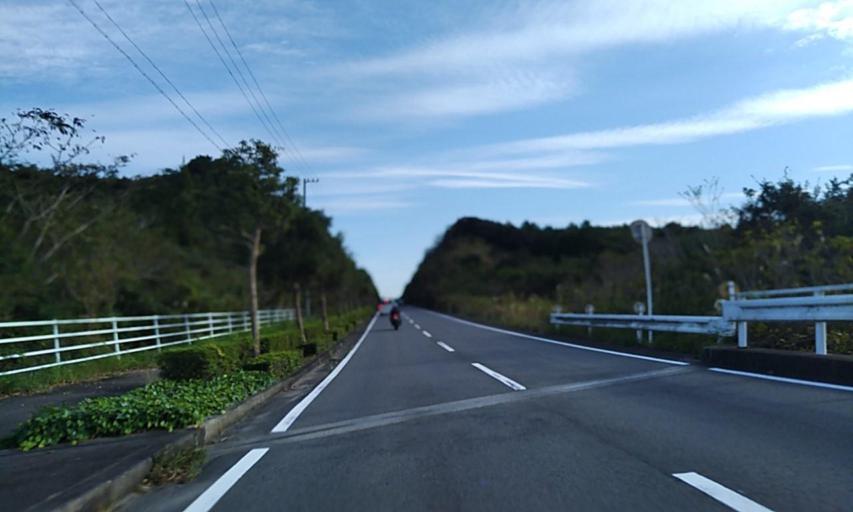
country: JP
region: Mie
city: Toba
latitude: 34.3575
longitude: 136.8050
